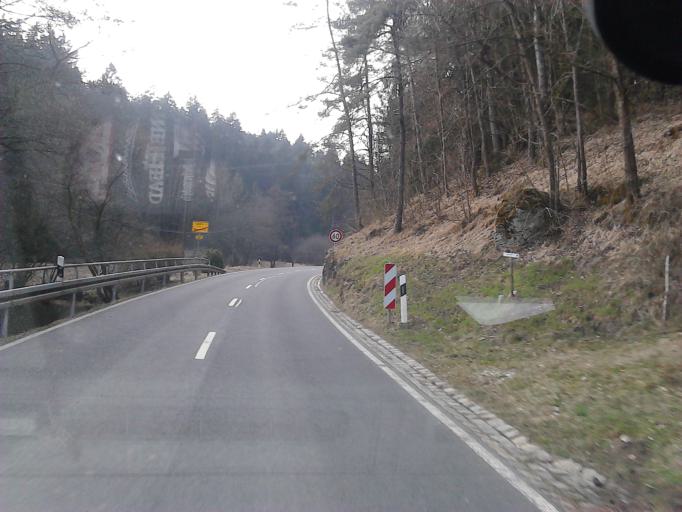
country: DE
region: Bavaria
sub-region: Upper Franconia
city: Stadelhofen
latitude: 49.9563
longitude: 11.2154
